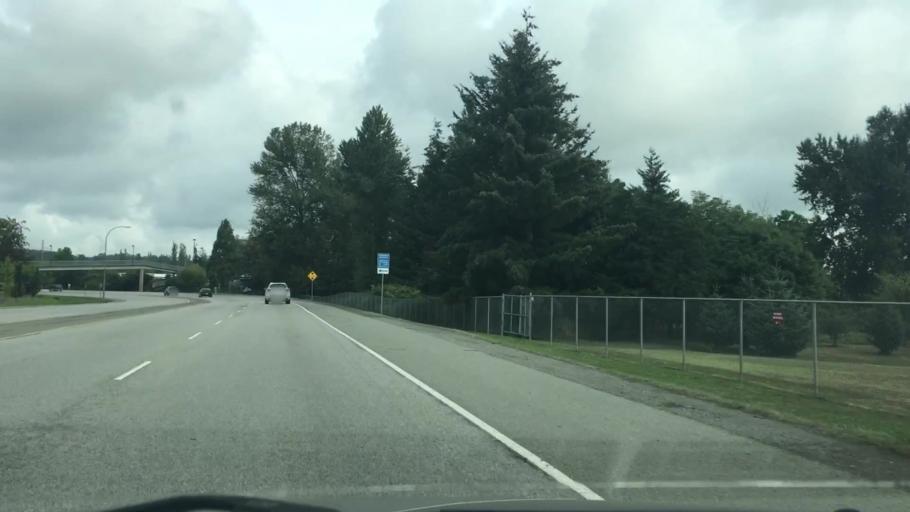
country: CA
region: British Columbia
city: Langley
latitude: 49.1082
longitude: -122.6427
